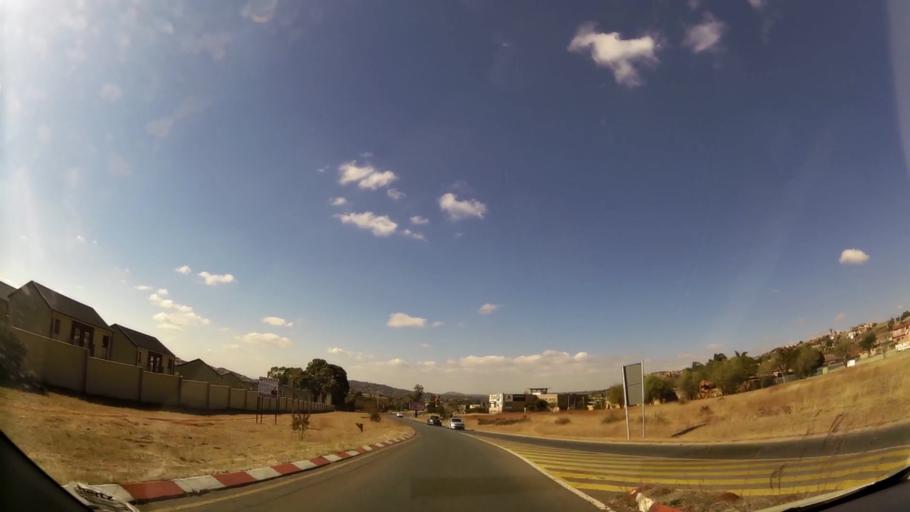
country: ZA
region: Gauteng
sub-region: West Rand District Municipality
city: Krugersdorp
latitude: -26.0881
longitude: 27.8163
